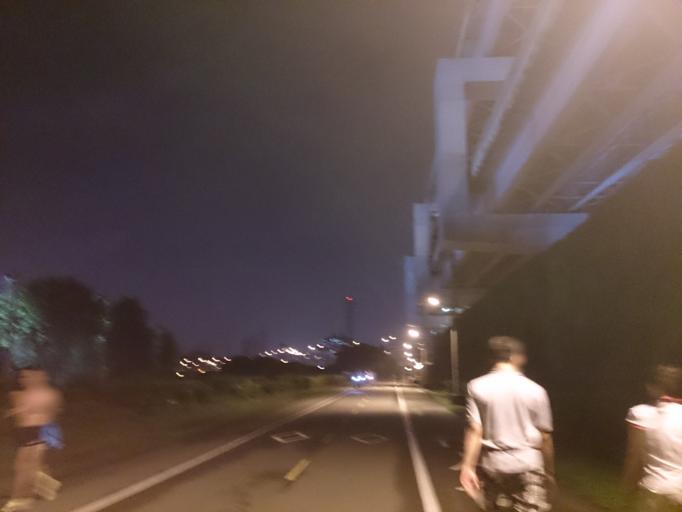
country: TW
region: Taipei
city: Taipei
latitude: 24.9994
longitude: 121.5351
